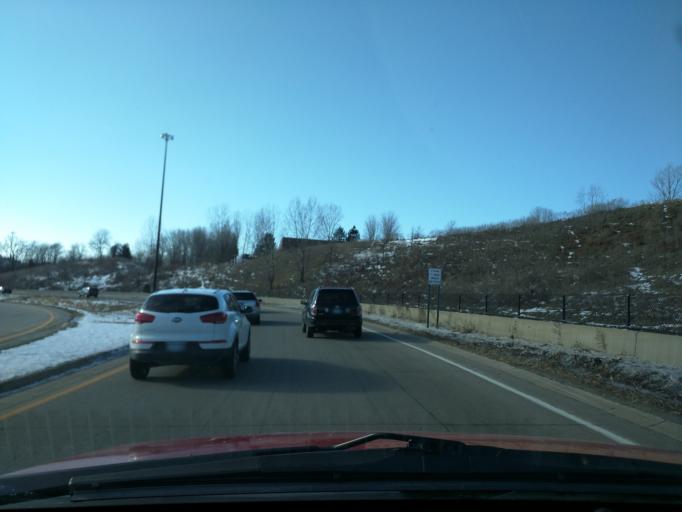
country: US
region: Minnesota
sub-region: Hennepin County
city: Eden Prairie
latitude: 44.8633
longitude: -93.4451
